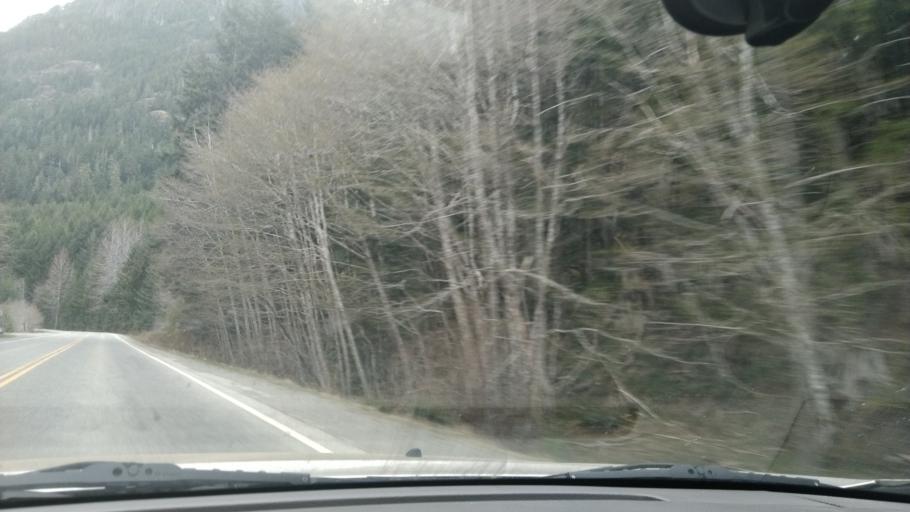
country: CA
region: British Columbia
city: Campbell River
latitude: 49.8541
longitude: -125.8344
